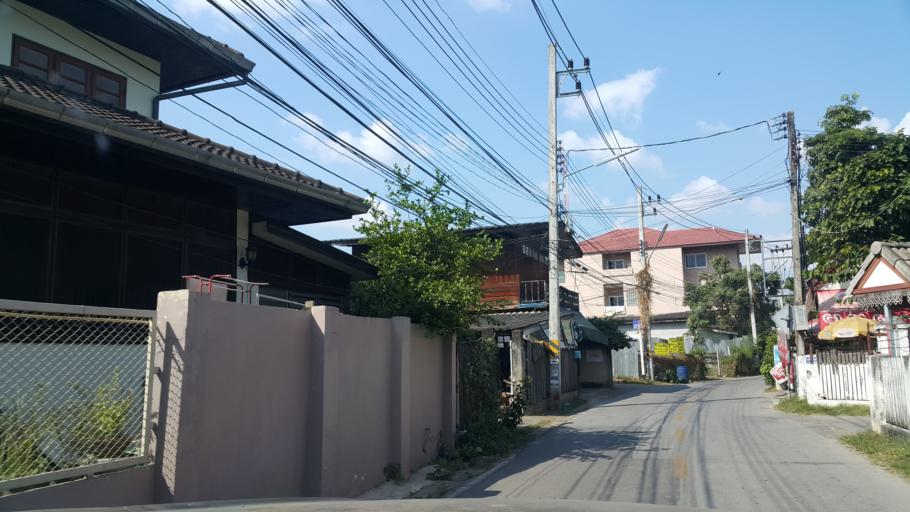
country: TH
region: Chiang Mai
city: Chiang Mai
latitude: 18.7939
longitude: 99.0030
